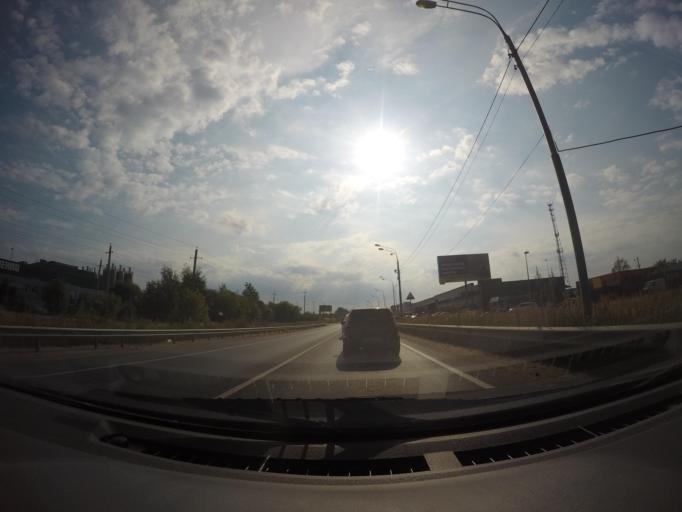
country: RU
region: Moskovskaya
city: Gzhel'
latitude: 55.6041
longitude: 38.4309
